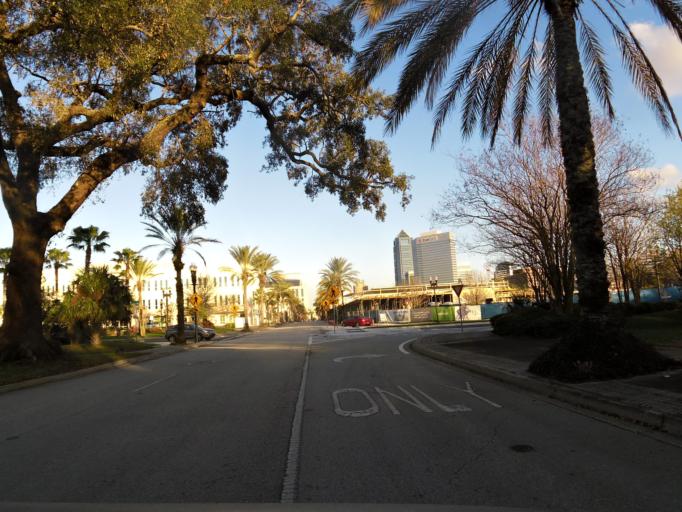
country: US
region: Florida
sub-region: Duval County
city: Jacksonville
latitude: 30.3313
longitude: -81.6700
